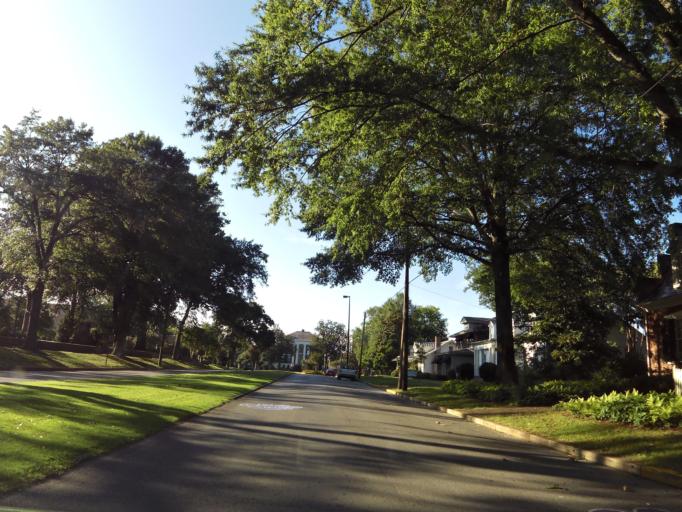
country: US
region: Alabama
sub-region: Lauderdale County
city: Florence
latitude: 34.8043
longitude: -87.6785
